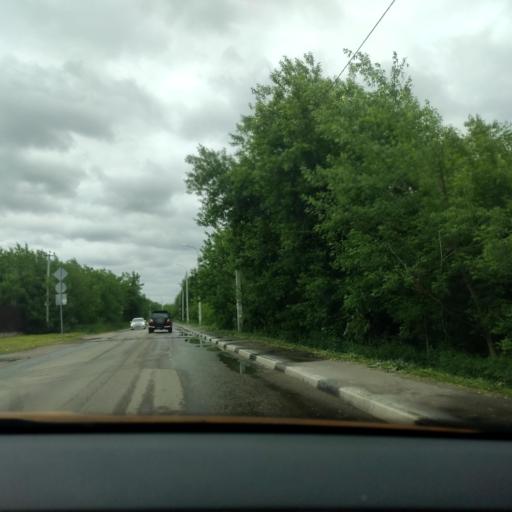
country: RU
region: Moskovskaya
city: Vereya
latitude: 55.6059
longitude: 38.0473
